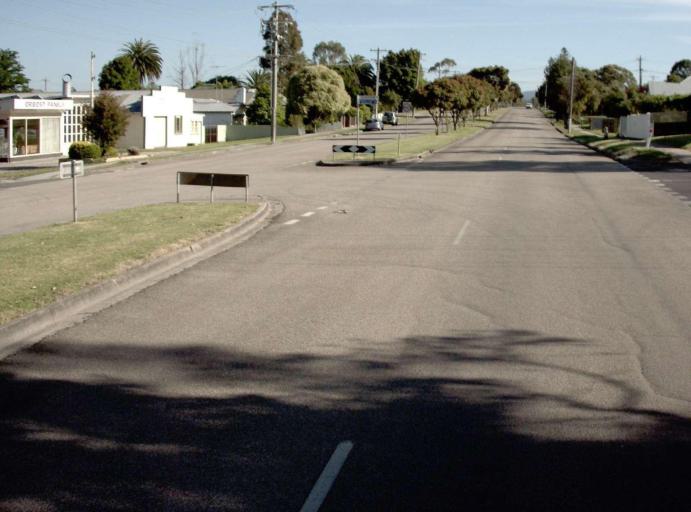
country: AU
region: Victoria
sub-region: East Gippsland
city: Lakes Entrance
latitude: -37.7026
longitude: 148.4561
